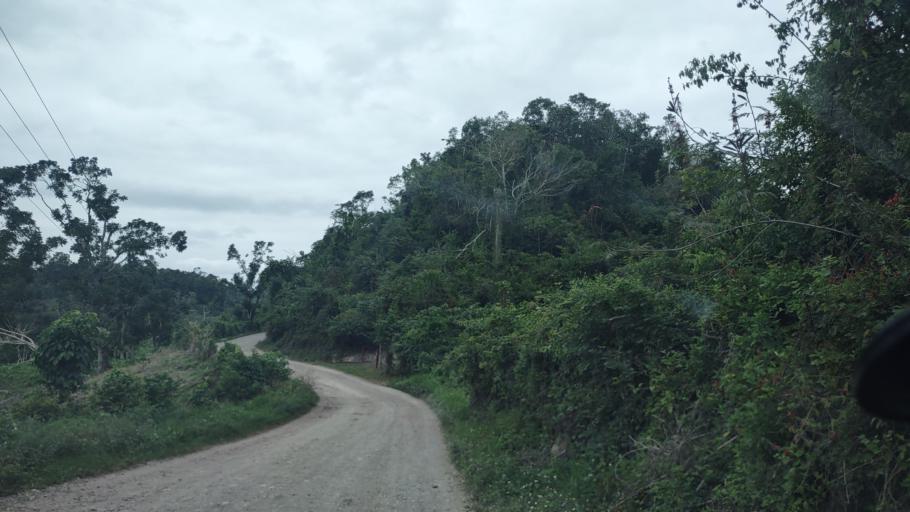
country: MX
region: Veracruz
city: Papantla de Olarte
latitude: 20.4372
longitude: -97.2751
